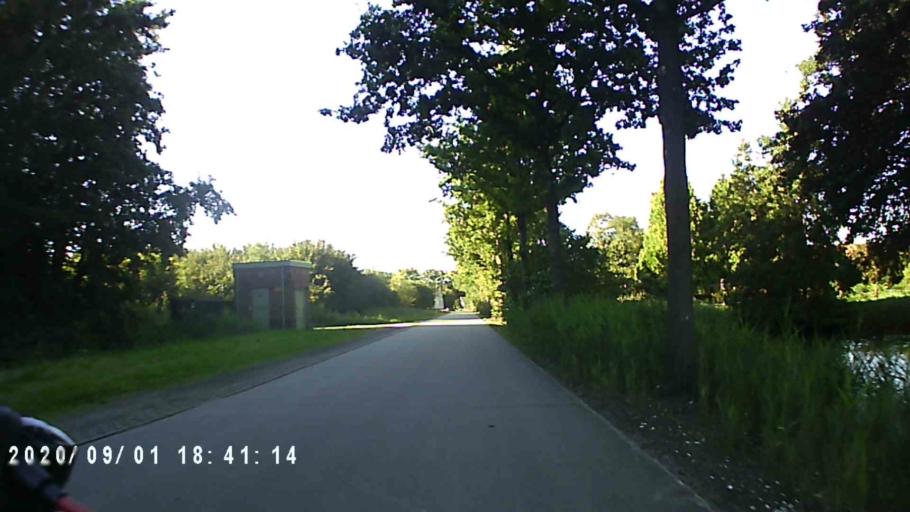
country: NL
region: Groningen
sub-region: Gemeente Hoogezand-Sappemeer
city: Sappemeer
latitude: 53.1478
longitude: 6.8239
